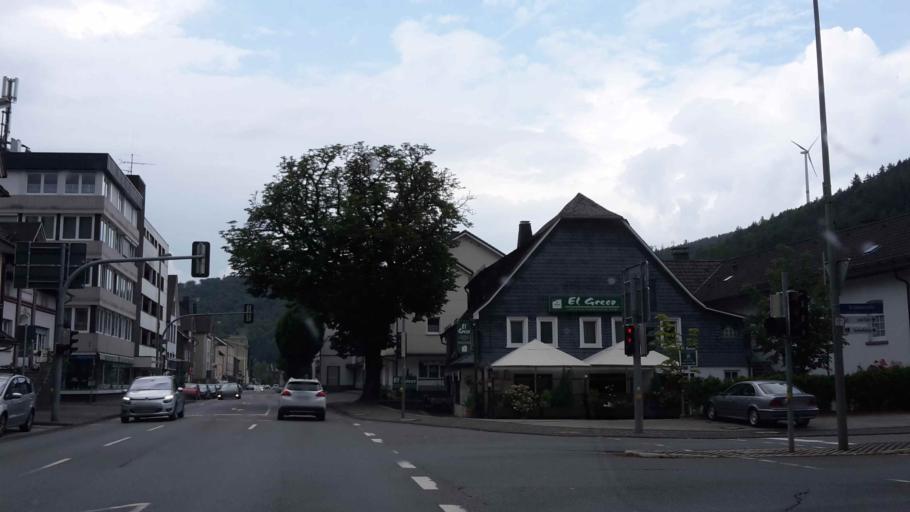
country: DE
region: North Rhine-Westphalia
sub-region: Regierungsbezirk Arnsberg
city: Lennestadt
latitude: 51.1233
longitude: 8.0684
